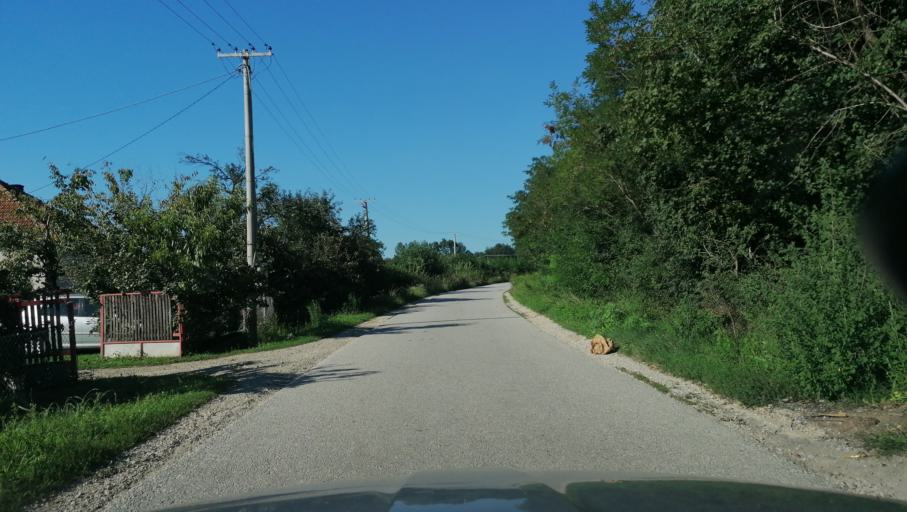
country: RS
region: Central Serbia
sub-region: Sumadijski Okrug
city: Knic
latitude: 43.8622
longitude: 20.6011
